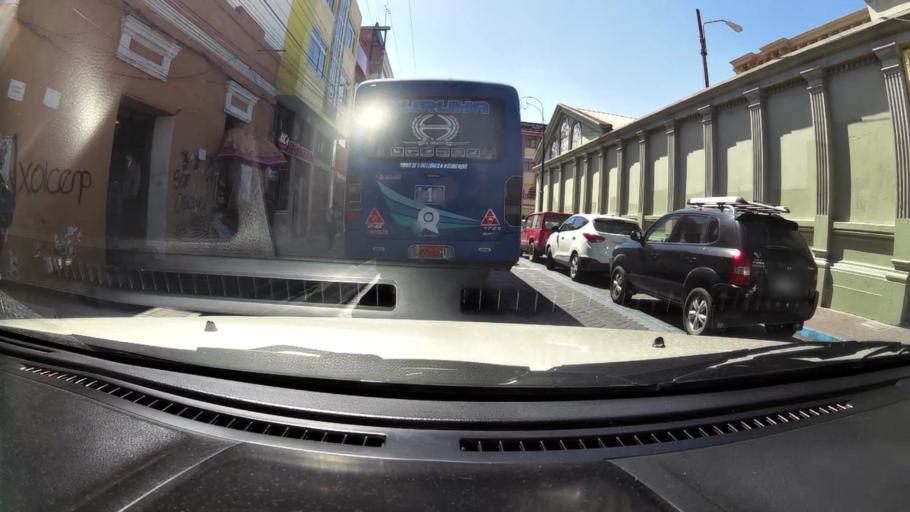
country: EC
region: Chimborazo
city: Riobamba
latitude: -1.6709
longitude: -78.6498
